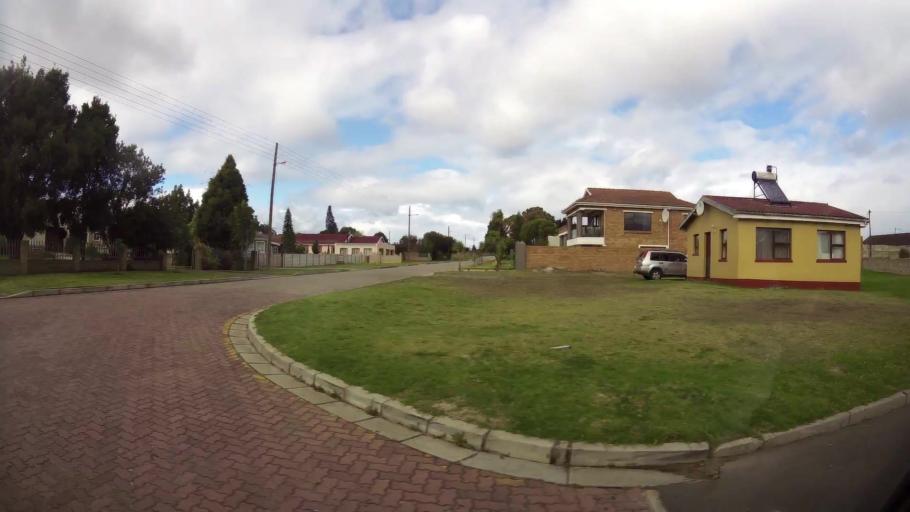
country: ZA
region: Western Cape
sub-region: Eden District Municipality
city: George
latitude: -34.0039
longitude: 22.4433
